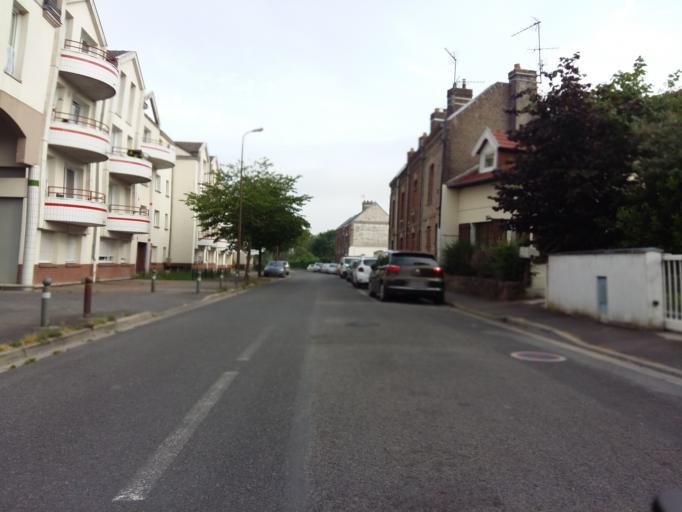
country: FR
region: Picardie
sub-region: Departement de la Somme
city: Amiens
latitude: 49.9076
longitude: 2.2894
